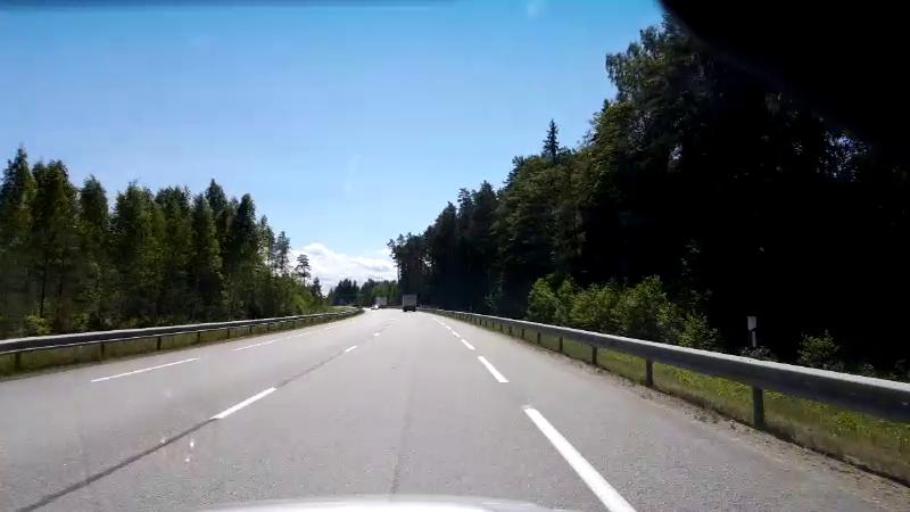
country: LV
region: Saulkrastu
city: Saulkrasti
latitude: 57.3440
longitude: 24.4429
